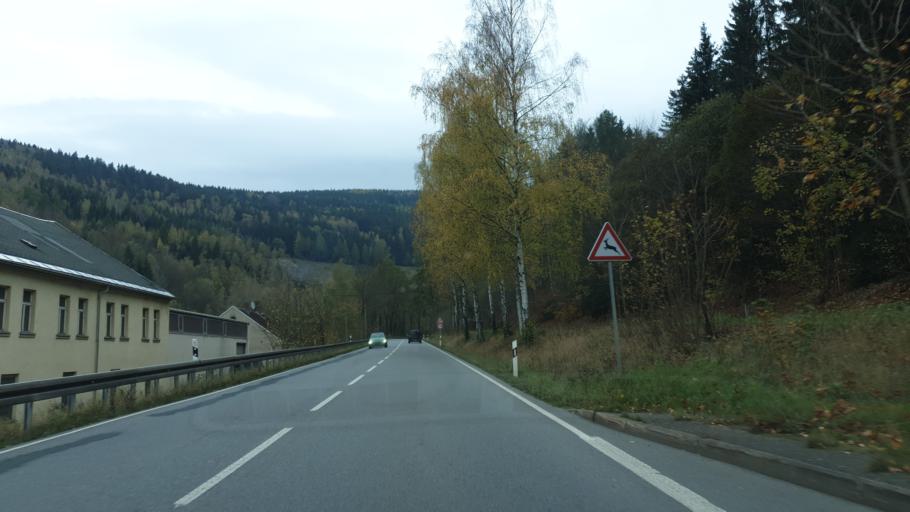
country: DE
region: Saxony
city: Schwarzenberg
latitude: 50.5102
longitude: 12.7737
